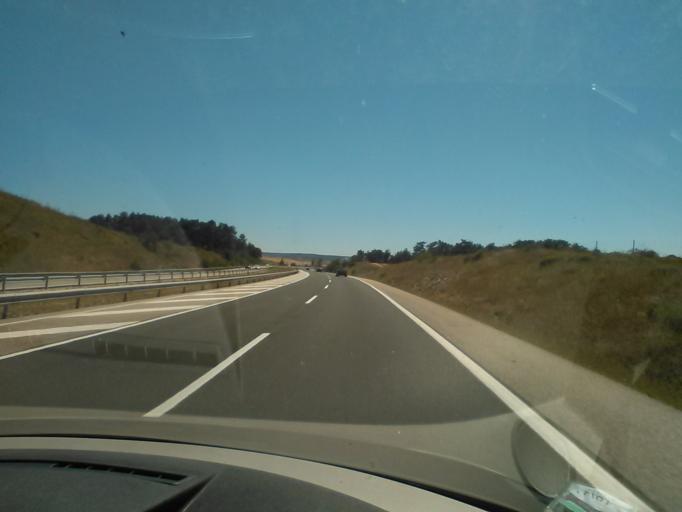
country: ES
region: Castille and Leon
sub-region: Provincia de Burgos
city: Fresno de Rodilla
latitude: 42.4356
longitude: -3.4985
